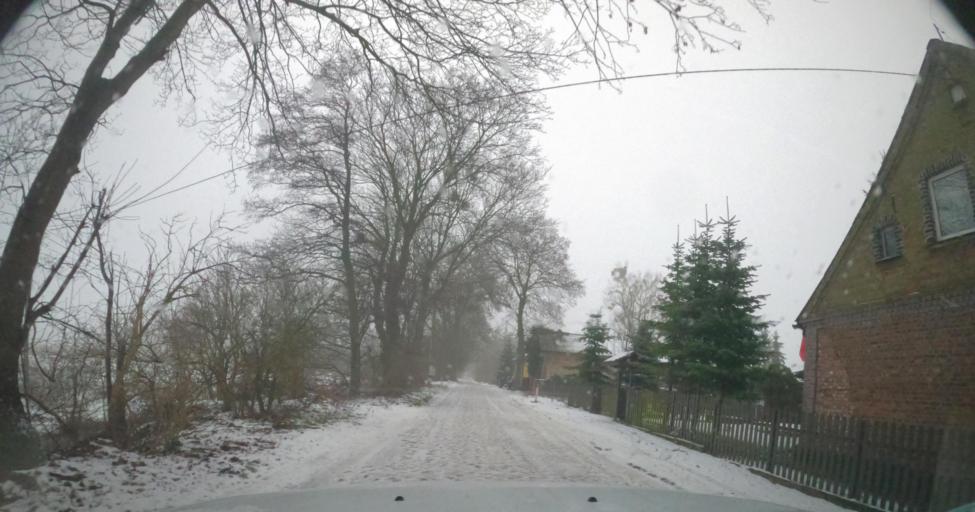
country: PL
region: West Pomeranian Voivodeship
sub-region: Powiat policki
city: Police
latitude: 53.5535
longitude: 14.6205
